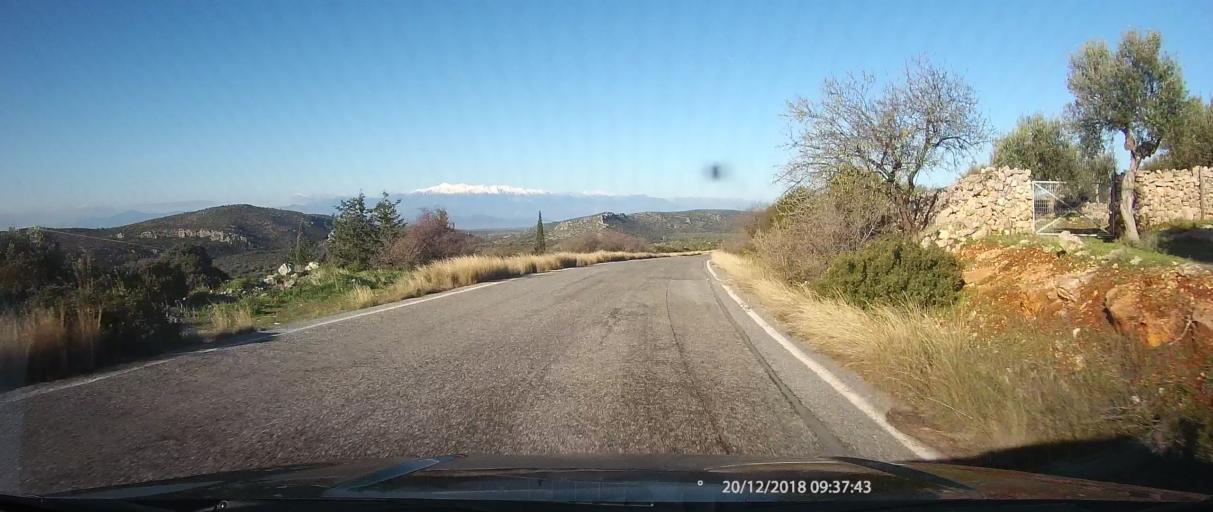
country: GR
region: Peloponnese
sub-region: Nomos Lakonias
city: Kato Glikovrisi
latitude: 36.9382
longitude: 22.8034
